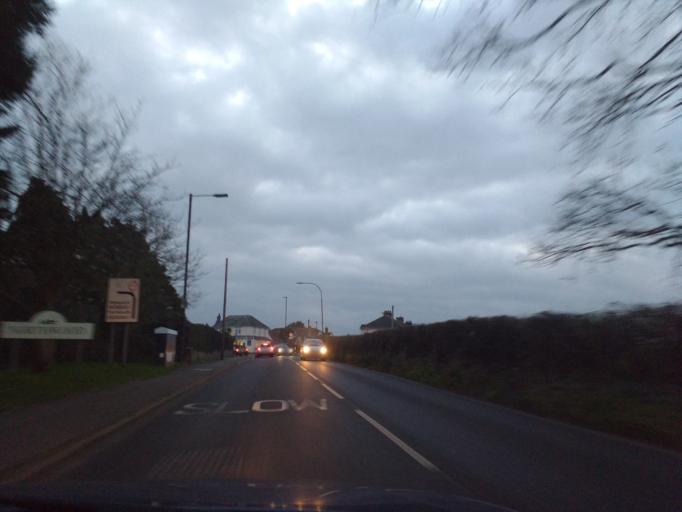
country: GB
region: England
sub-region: Isle of Wight
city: Northwood
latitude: 50.7458
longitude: -1.3127
